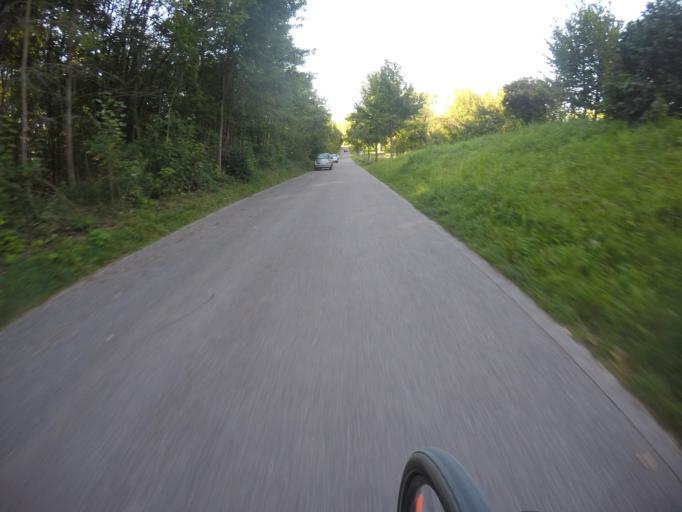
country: DE
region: Baden-Wuerttemberg
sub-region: Regierungsbezirk Stuttgart
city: Stuttgart Feuerbach
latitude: 48.8238
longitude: 9.1519
